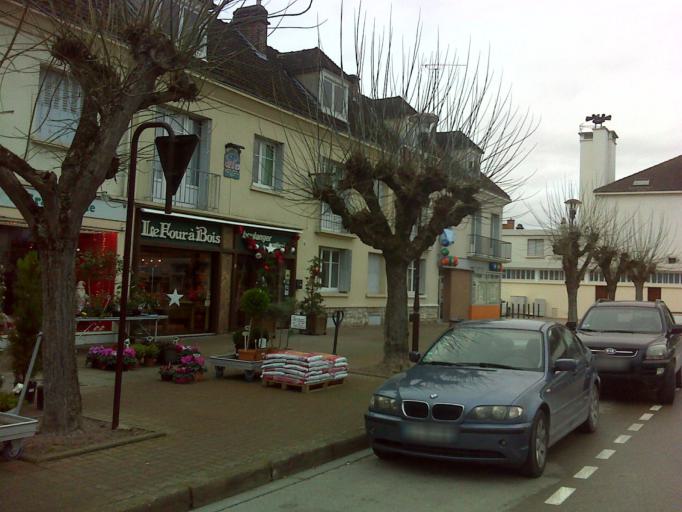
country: FR
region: Champagne-Ardenne
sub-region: Departement de l'Aube
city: Arcis-sur-Aube
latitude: 48.5361
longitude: 4.1422
